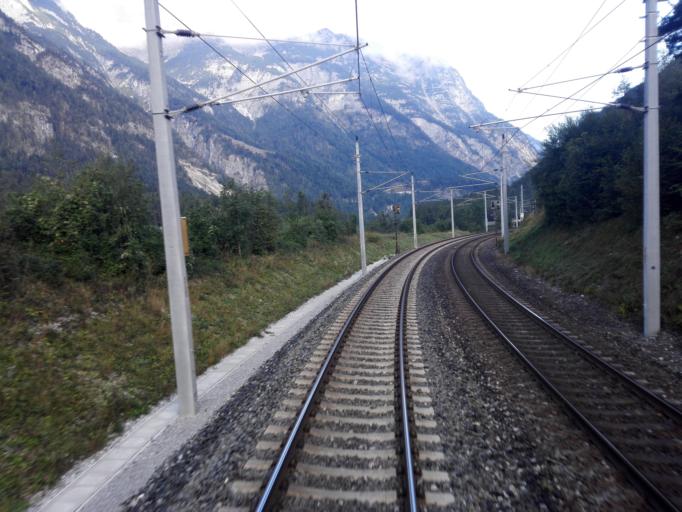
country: AT
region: Salzburg
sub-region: Politischer Bezirk Sankt Johann im Pongau
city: Werfen
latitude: 47.5079
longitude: 13.1716
